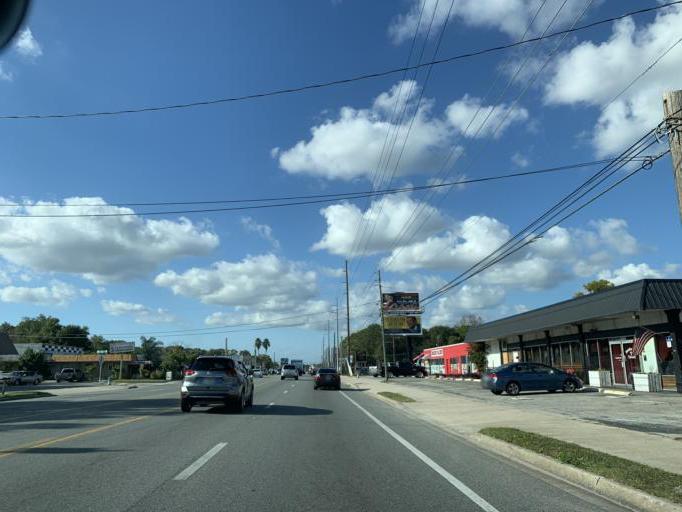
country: US
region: Florida
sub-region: Orange County
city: Fairview Shores
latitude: 28.6067
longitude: -81.4107
